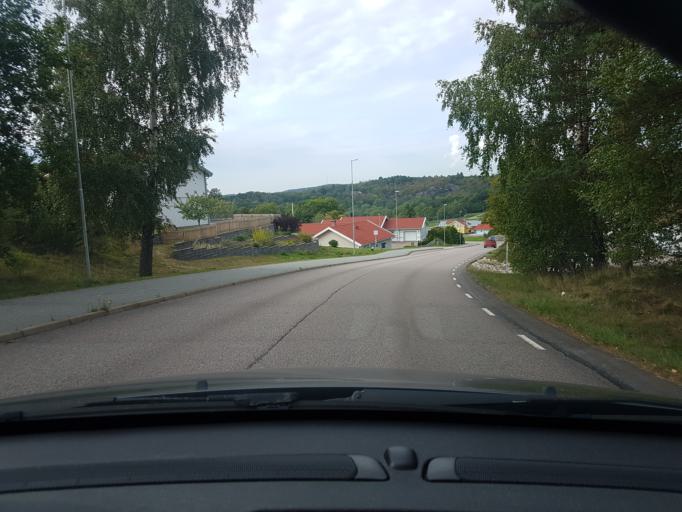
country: SE
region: Vaestra Goetaland
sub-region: Ale Kommun
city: Surte
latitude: 57.8509
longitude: 12.0323
